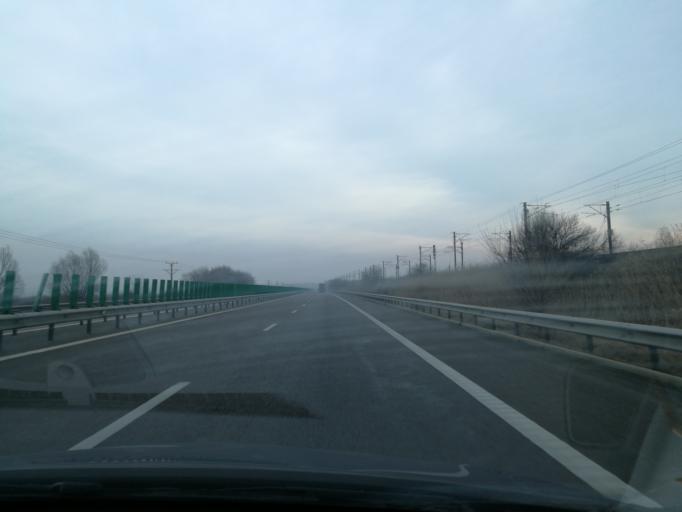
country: RO
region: Constanta
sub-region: Oras Cernavoda
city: Cernavoda
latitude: 44.3511
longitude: 27.9750
